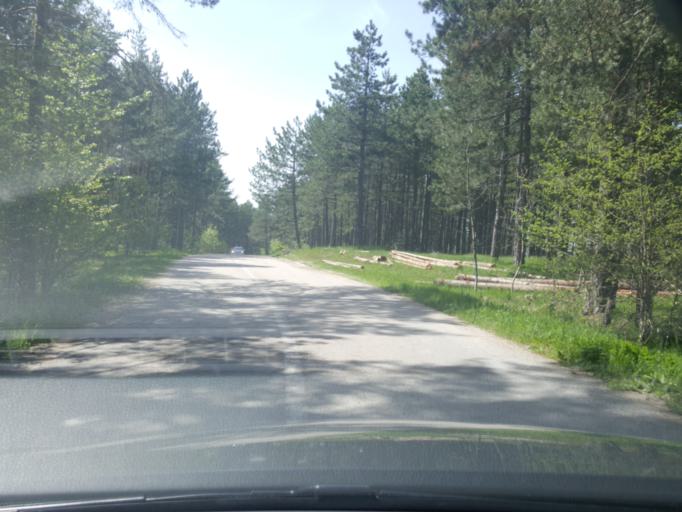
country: RS
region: Central Serbia
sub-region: Zlatiborski Okrug
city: Bajina Basta
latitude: 43.8887
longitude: 19.5355
